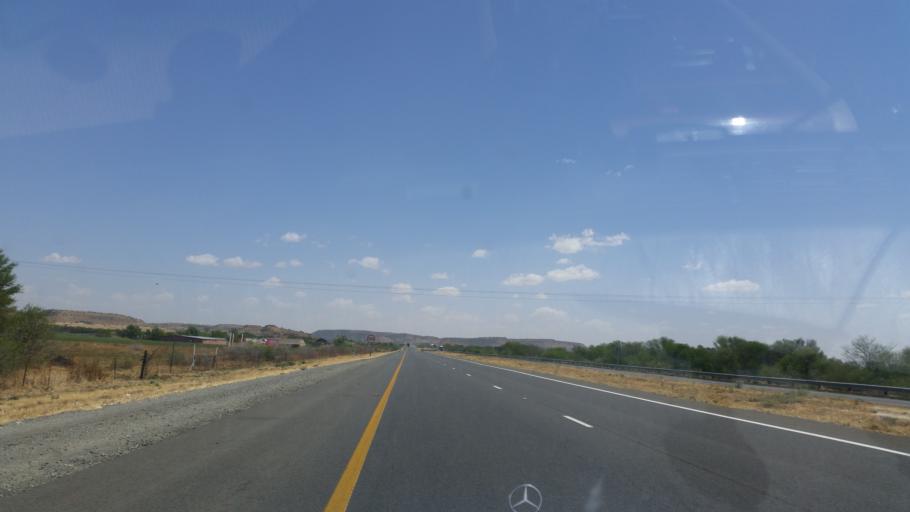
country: ZA
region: Orange Free State
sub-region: Mangaung Metropolitan Municipality
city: Bloemfontein
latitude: -28.9671
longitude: 26.3396
